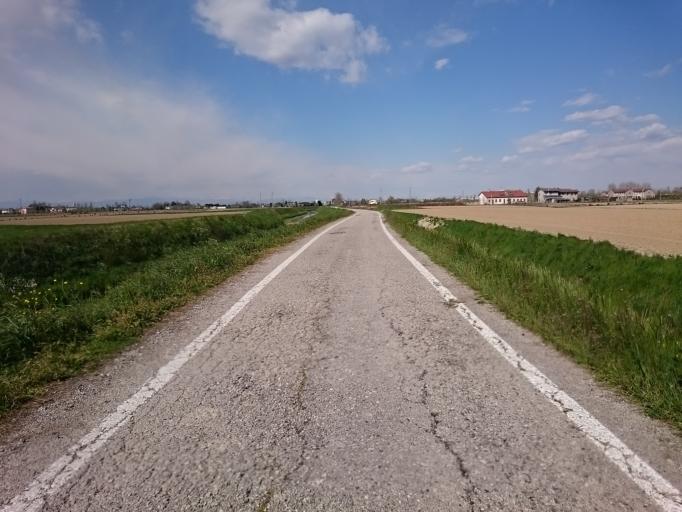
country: IT
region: Veneto
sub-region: Provincia di Padova
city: Legnaro
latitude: 45.3329
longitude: 11.9457
